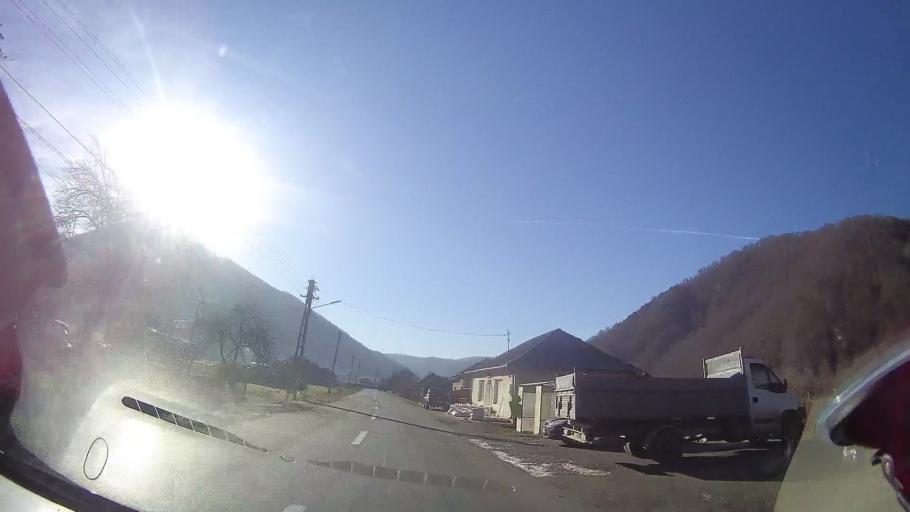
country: RO
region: Bihor
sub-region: Comuna Bulz
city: Bulz
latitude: 46.9430
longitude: 22.6725
